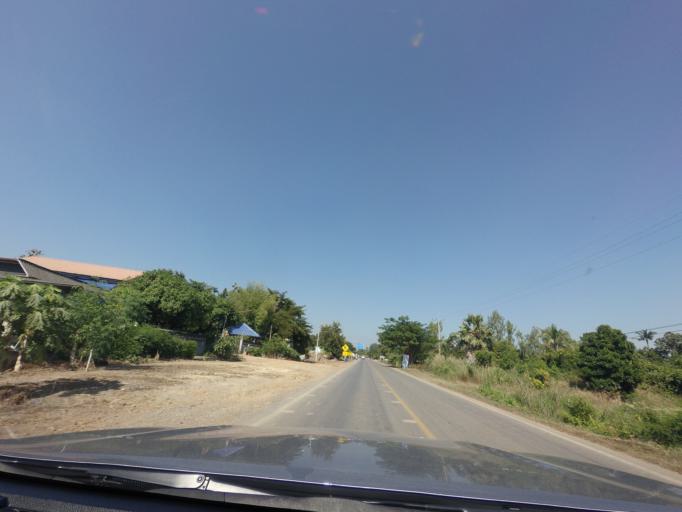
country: TH
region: Sukhothai
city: Sawankhalok
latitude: 17.3922
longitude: 99.7948
